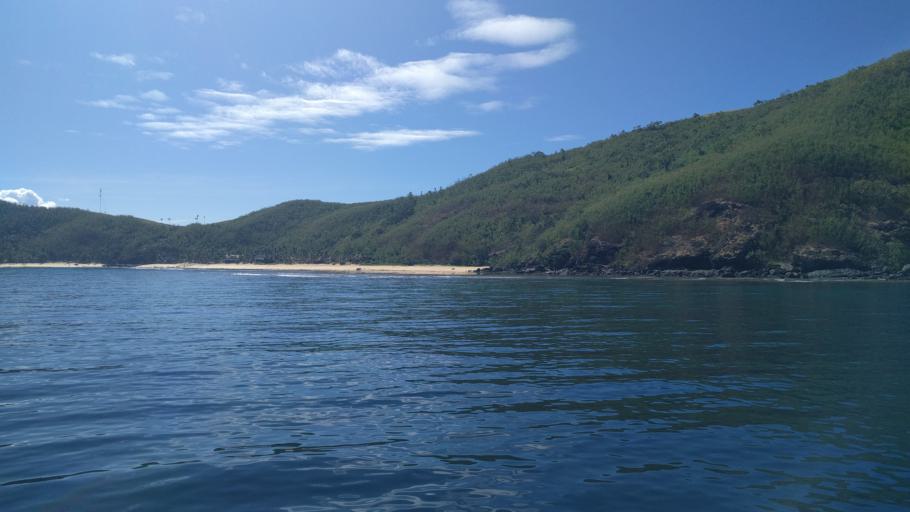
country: FJ
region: Western
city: Lautoka
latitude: -17.2809
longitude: 177.1032
